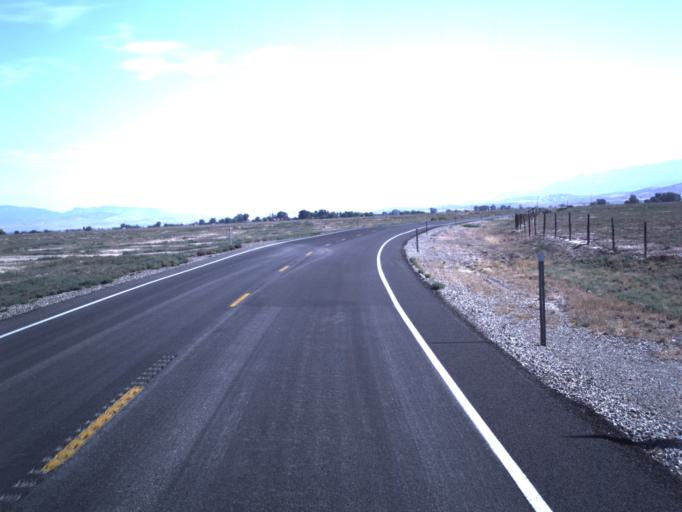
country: US
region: Utah
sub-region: Sevier County
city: Salina
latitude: 39.0331
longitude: -111.8401
